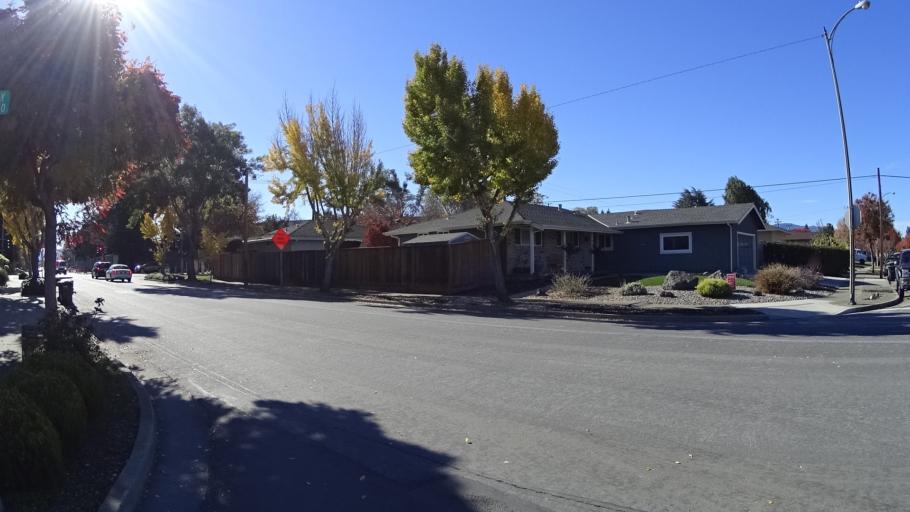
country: US
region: California
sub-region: Santa Clara County
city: Cupertino
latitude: 37.3385
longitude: -122.0053
